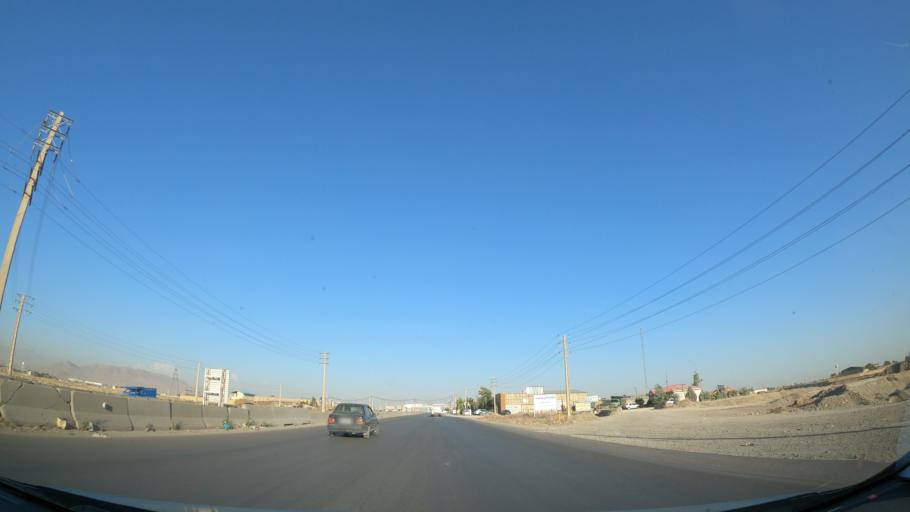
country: IR
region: Alborz
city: Hashtgerd
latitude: 35.9195
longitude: 50.7497
